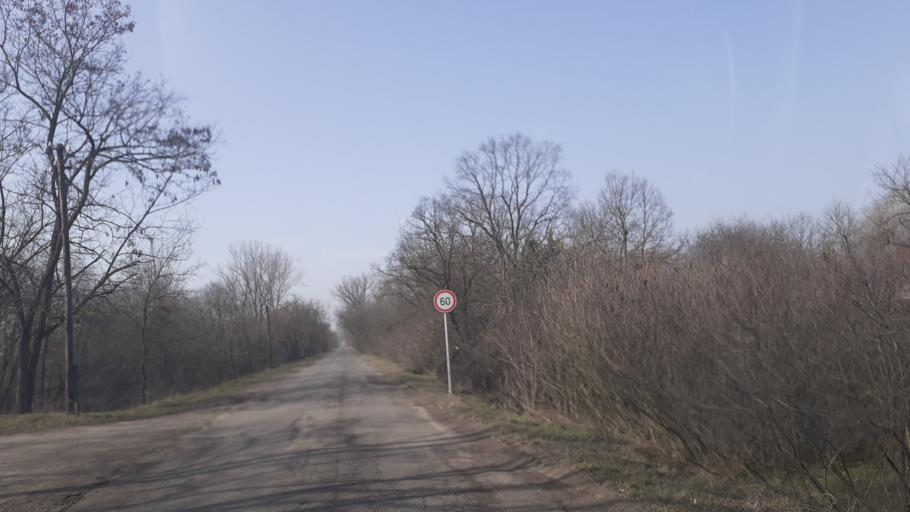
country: HU
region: Pest
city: Dabas
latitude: 47.0653
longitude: 19.2753
